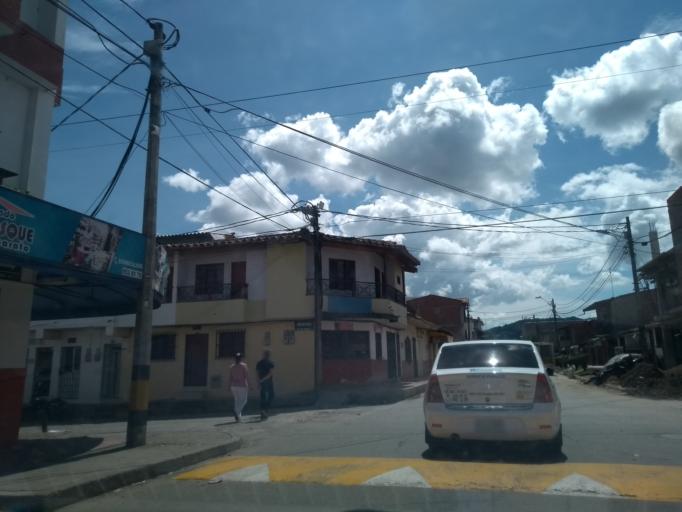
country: CO
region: Antioquia
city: La Ceja
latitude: 6.0337
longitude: -75.4277
